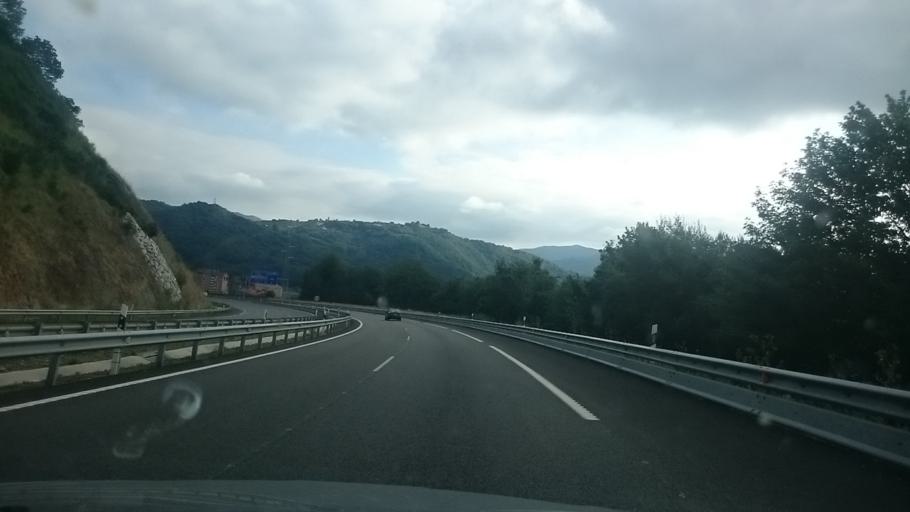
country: ES
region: Asturias
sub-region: Province of Asturias
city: Sama
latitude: 43.3337
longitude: -5.7126
